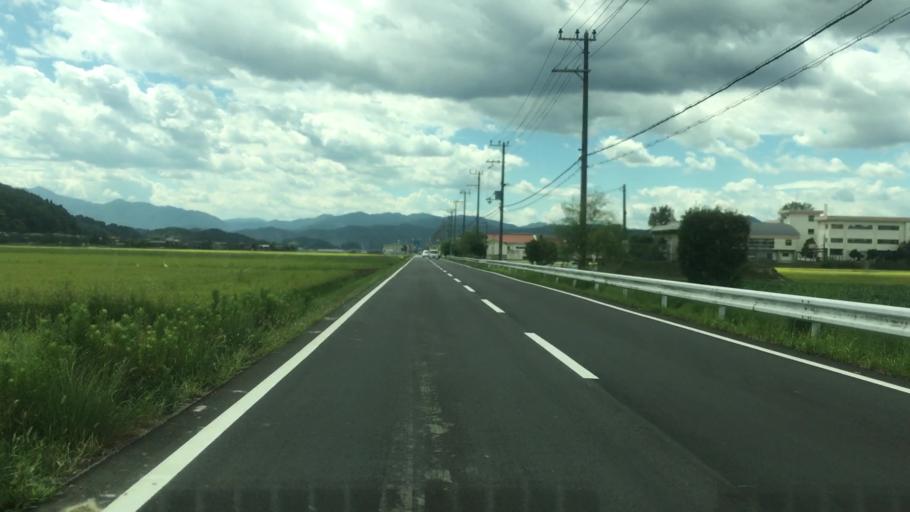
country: JP
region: Hyogo
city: Toyooka
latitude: 35.5326
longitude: 134.8397
